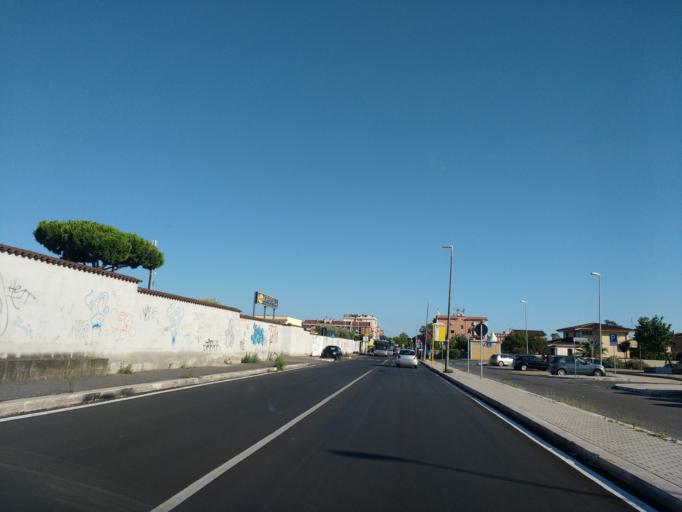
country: IT
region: Latium
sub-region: Citta metropolitana di Roma Capitale
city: Acilia-Castel Fusano-Ostia Antica
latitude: 41.7723
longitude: 12.3546
